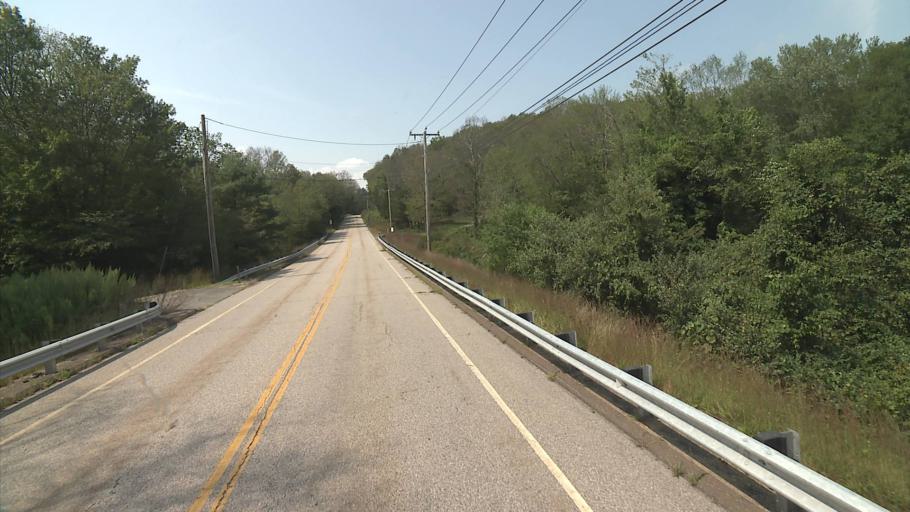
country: US
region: Connecticut
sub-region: Middlesex County
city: Deep River Center
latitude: 41.4233
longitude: -72.4012
